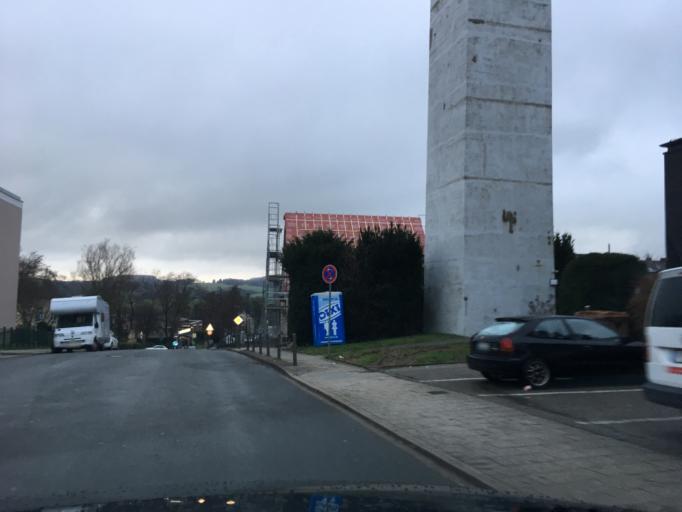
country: DE
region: North Rhine-Westphalia
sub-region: Regierungsbezirk Dusseldorf
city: Velbert
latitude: 51.3048
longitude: 7.1016
